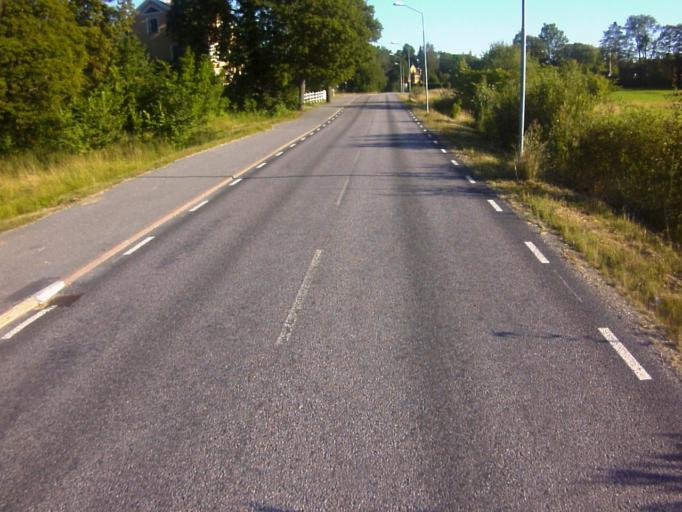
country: SE
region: Soedermanland
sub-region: Eskilstuna Kommun
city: Hallbybrunn
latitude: 59.3967
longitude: 16.4346
